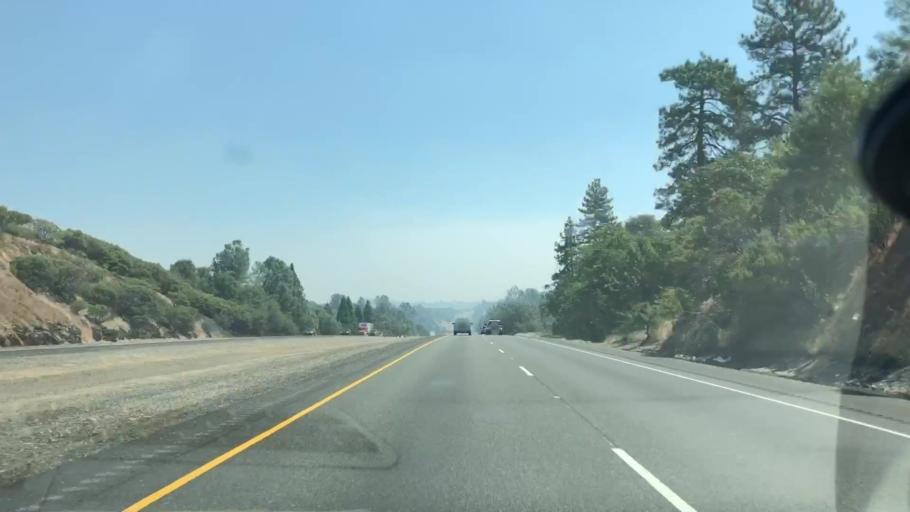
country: US
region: California
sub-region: El Dorado County
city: Deer Park
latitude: 38.7000
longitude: -120.8697
